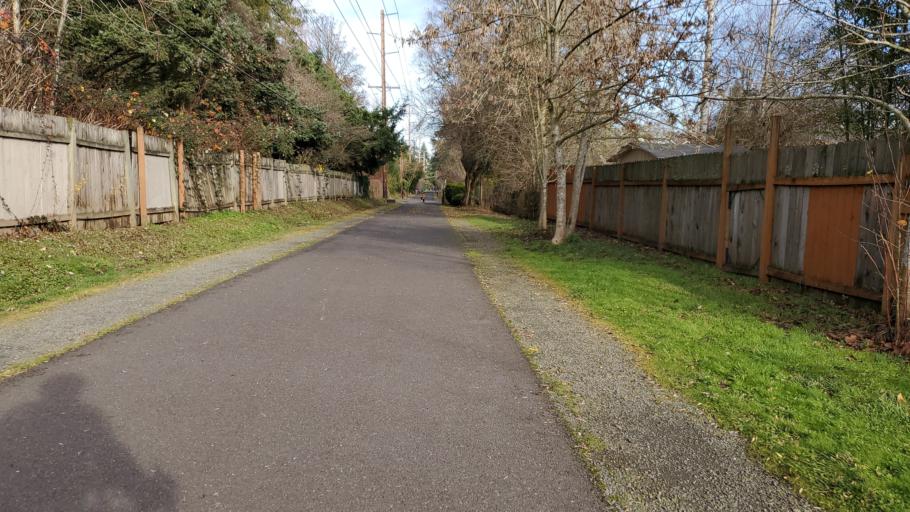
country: US
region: Oregon
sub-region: Clackamas County
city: Oak Grove
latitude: 45.4244
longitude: -122.6405
